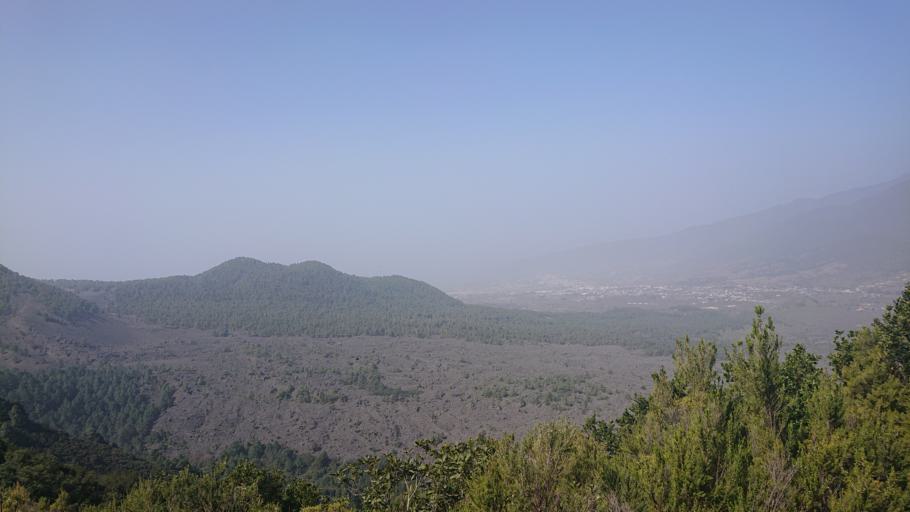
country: ES
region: Canary Islands
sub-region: Provincia de Santa Cruz de Tenerife
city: Brena Baja
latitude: 28.6322
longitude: -17.8266
